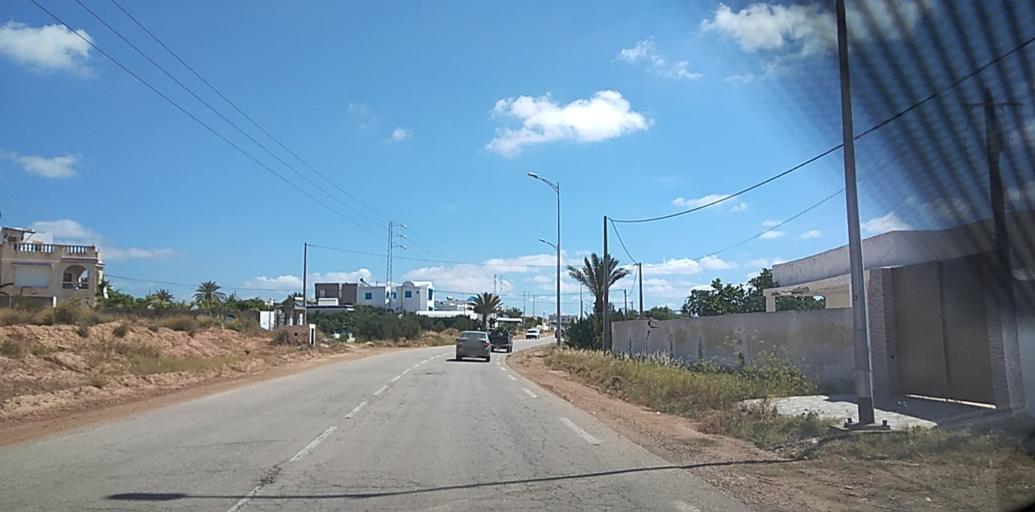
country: TN
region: Safaqis
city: Al Qarmadah
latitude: 34.6746
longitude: 11.1470
